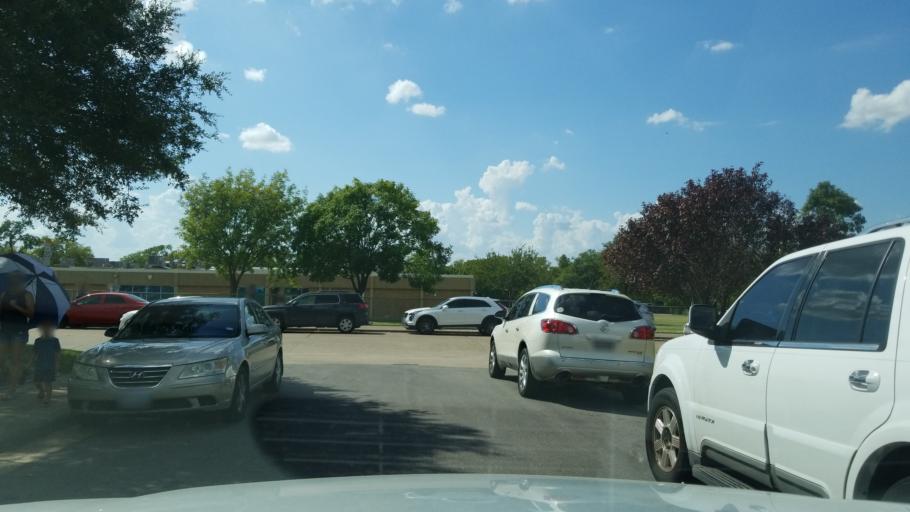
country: US
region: Texas
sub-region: Dallas County
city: Addison
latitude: 32.9605
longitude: -96.7938
